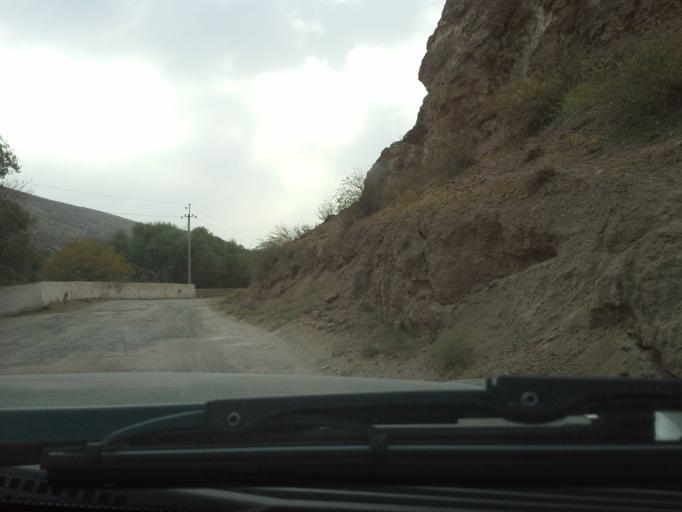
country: UZ
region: Qashqadaryo
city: Qorashina
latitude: 37.9384
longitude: 66.5345
